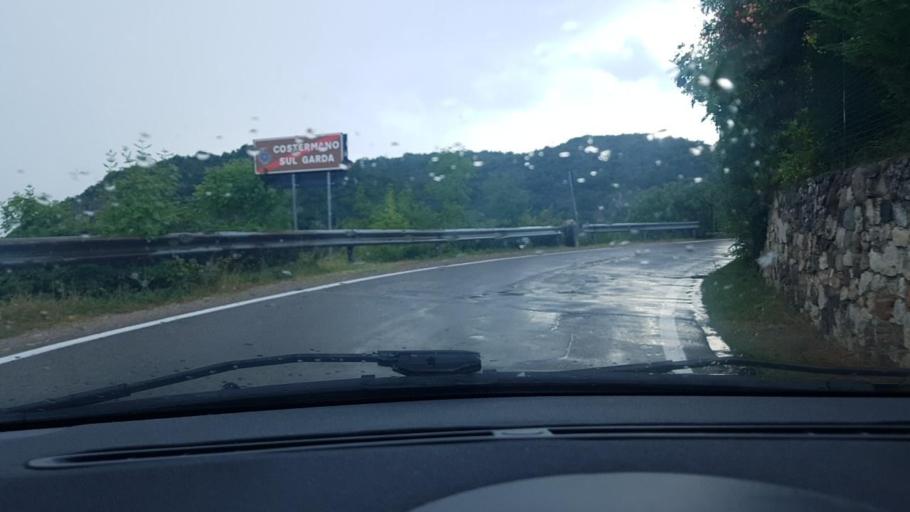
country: IT
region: Veneto
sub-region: Provincia di Verona
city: Garda
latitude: 45.5913
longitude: 10.7017
